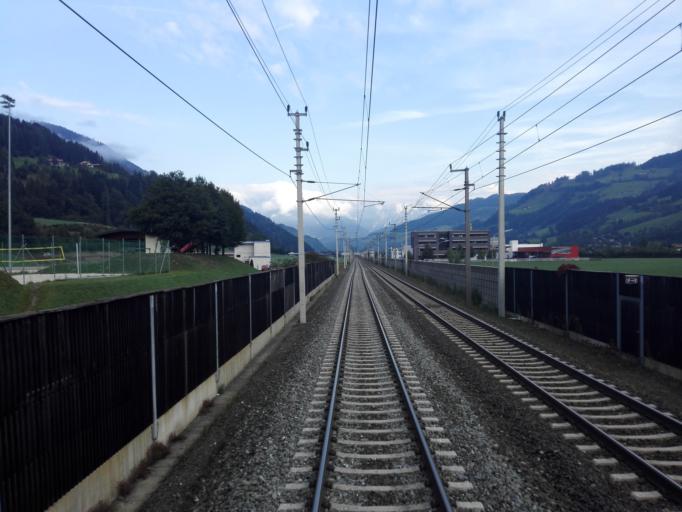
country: AT
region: Salzburg
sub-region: Politischer Bezirk Sankt Johann im Pongau
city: Sankt Johann im Pongau
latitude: 47.3592
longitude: 13.2028
